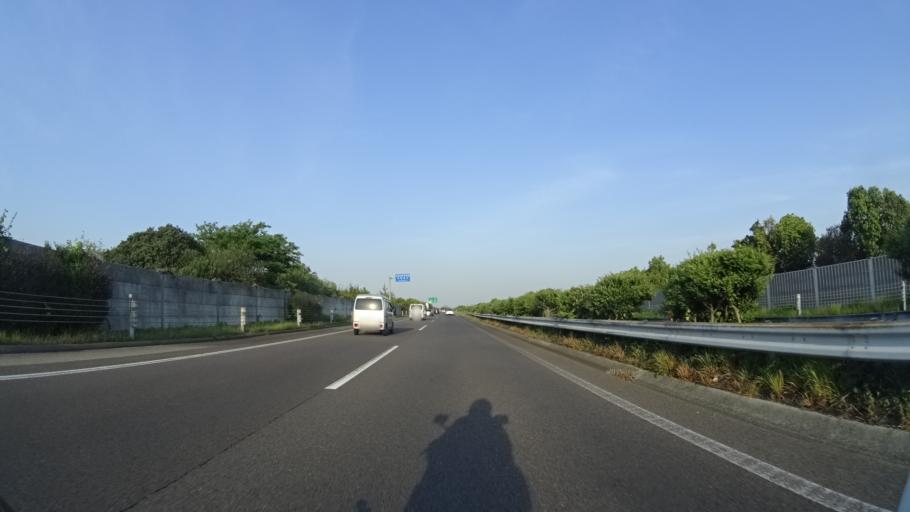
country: JP
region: Kagawa
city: Tadotsu
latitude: 34.2416
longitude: 133.7755
